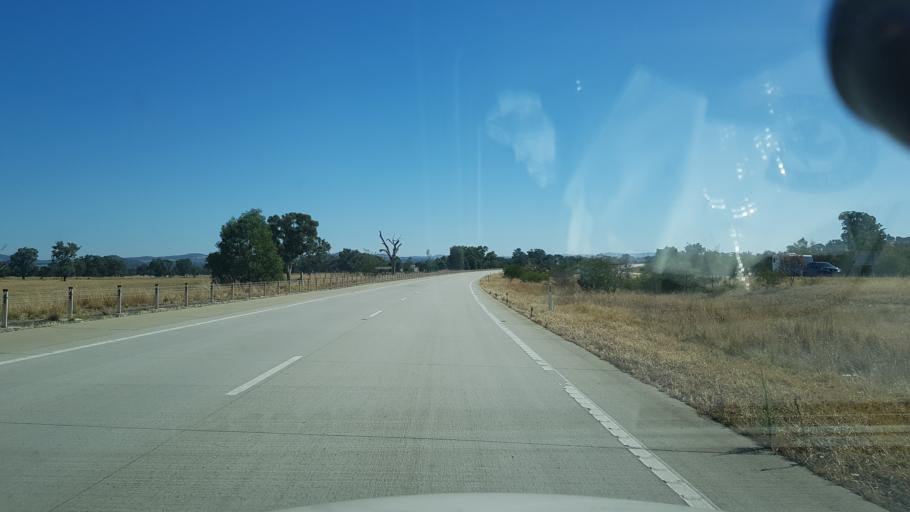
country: AU
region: New South Wales
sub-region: Albury Municipality
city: Lavington
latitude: -35.9271
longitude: 147.0837
